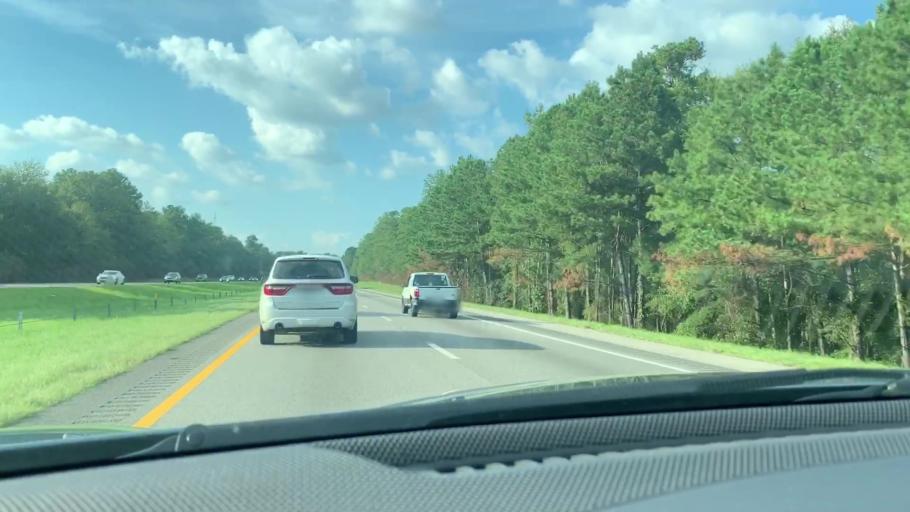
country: US
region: South Carolina
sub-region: Calhoun County
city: Oak Grove
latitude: 33.6866
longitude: -80.9074
